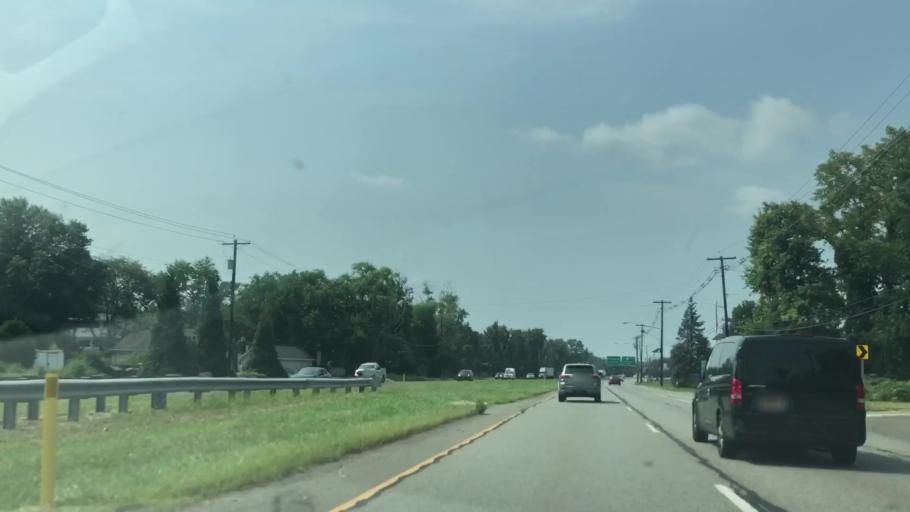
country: US
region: New Jersey
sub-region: Essex County
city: Fairfield
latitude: 40.8735
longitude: -74.3032
